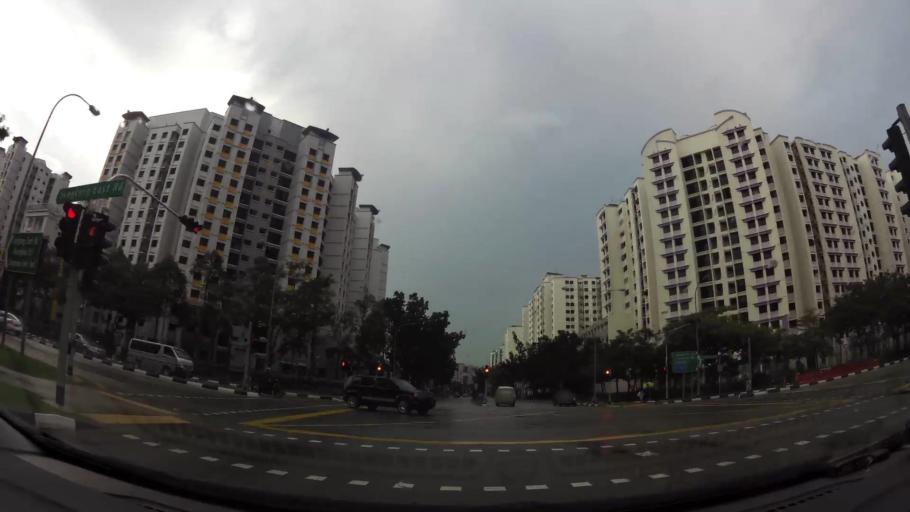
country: MY
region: Johor
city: Kampung Pasir Gudang Baru
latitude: 1.3895
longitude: 103.8925
